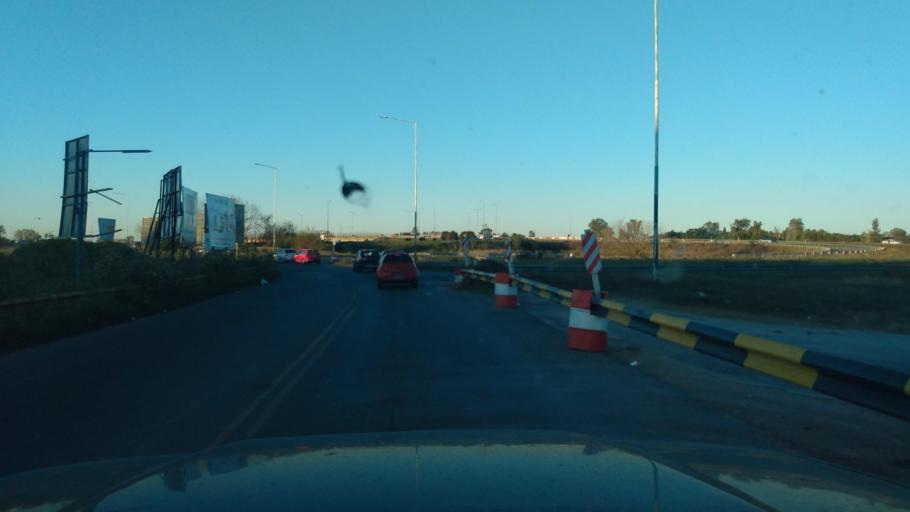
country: AR
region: Buenos Aires
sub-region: Partido de Merlo
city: Merlo
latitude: -34.6304
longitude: -58.7250
